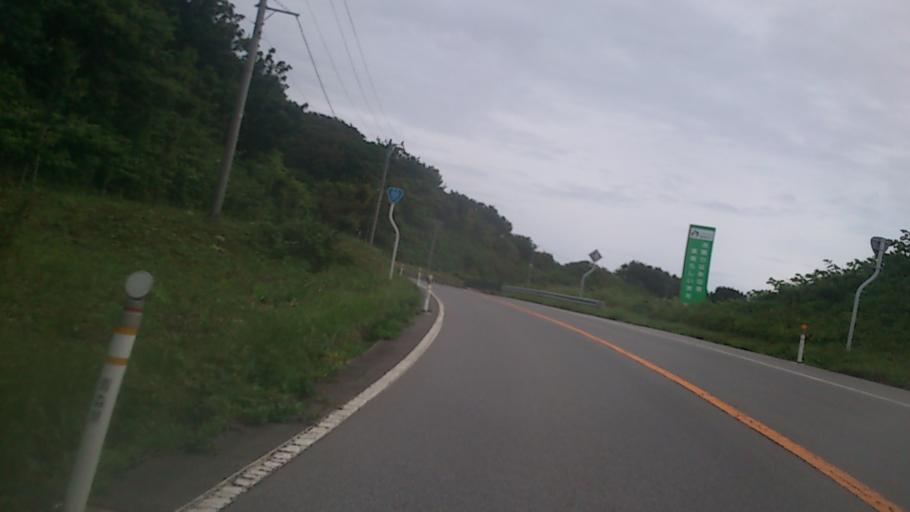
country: JP
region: Akita
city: Noshiromachi
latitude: 40.4321
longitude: 139.9409
